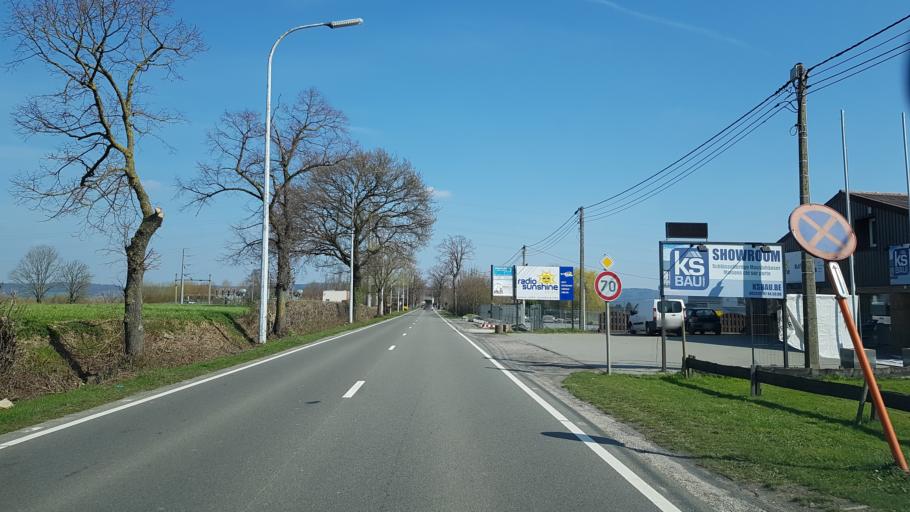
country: BE
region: Wallonia
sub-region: Province de Liege
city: Welkenraedt
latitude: 50.6935
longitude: 5.9649
